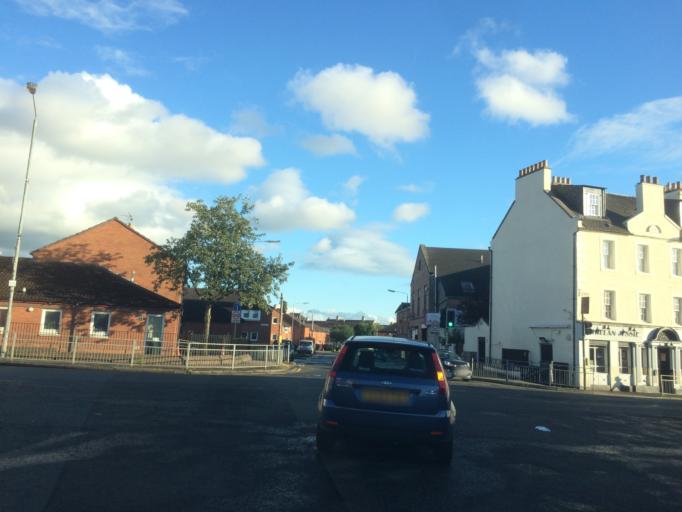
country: GB
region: Scotland
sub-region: Glasgow City
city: Glasgow
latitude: 55.8559
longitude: -4.2328
